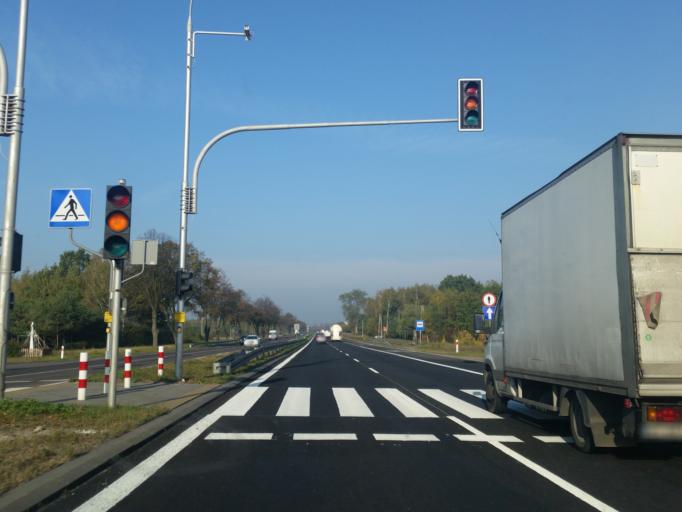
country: PL
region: Masovian Voivodeship
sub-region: Powiat plonski
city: Zaluski
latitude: 52.5804
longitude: 20.4732
